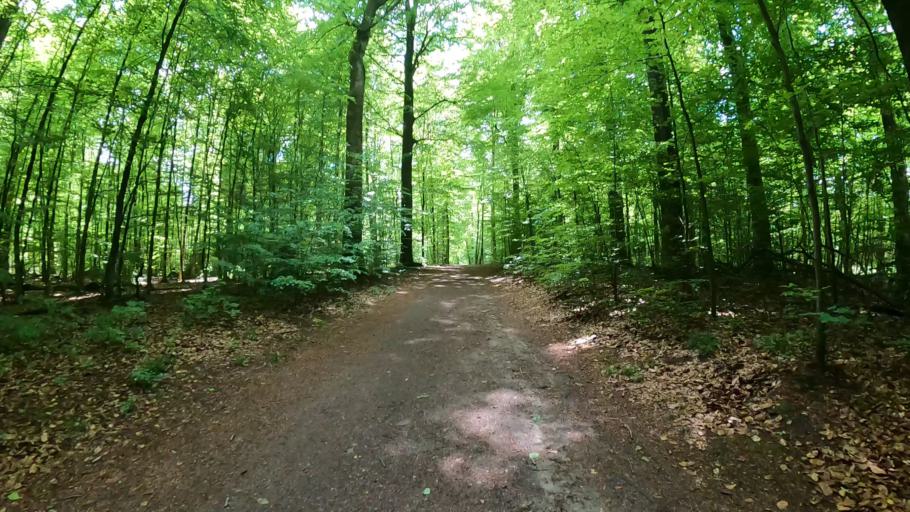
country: DE
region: Hamburg
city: Wohldorf-Ohlstedt
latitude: 53.7067
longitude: 10.1329
